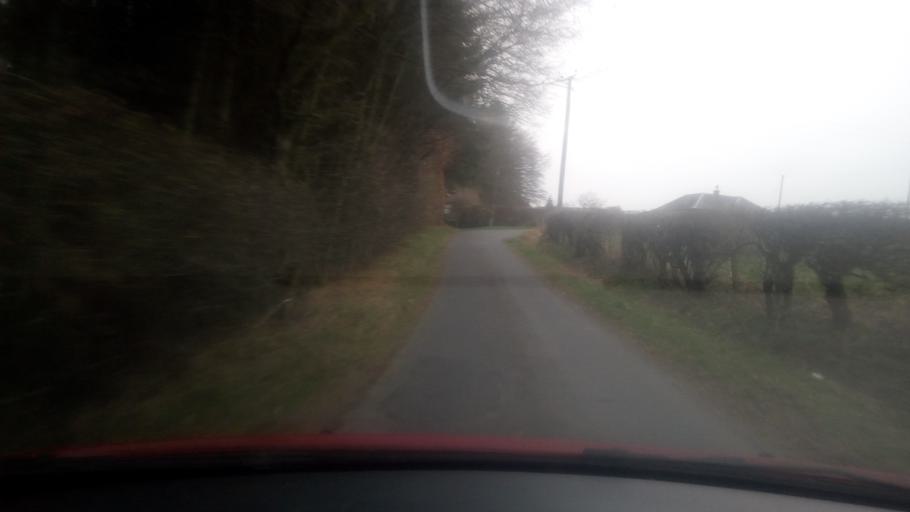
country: GB
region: Scotland
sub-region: The Scottish Borders
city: Hawick
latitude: 55.4401
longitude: -2.6914
